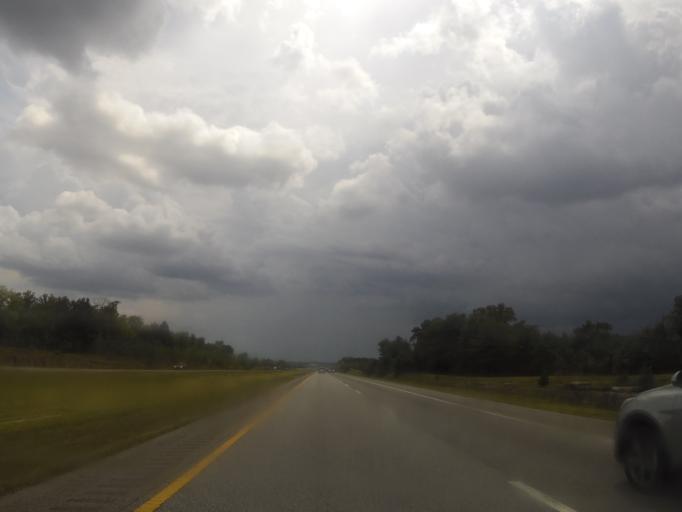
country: US
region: Tennessee
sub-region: Wilson County
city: Rural Hill
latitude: 36.0821
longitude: -86.4284
